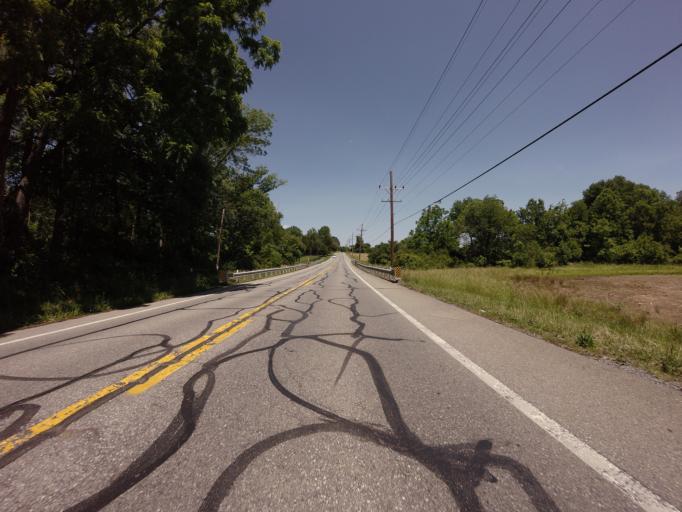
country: US
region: Maryland
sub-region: Frederick County
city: Brunswick
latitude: 39.3479
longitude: -77.6067
